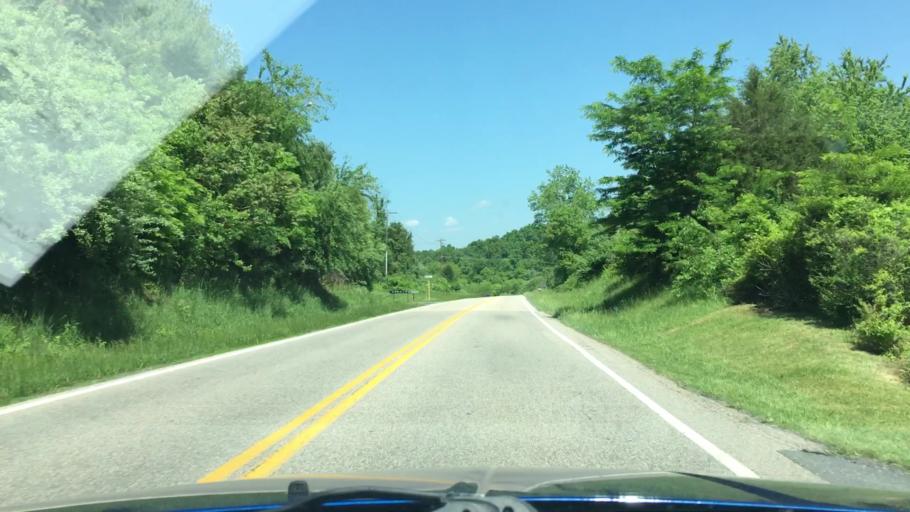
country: US
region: Virginia
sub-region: City of Staunton
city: Staunton
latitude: 38.1853
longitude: -79.1010
